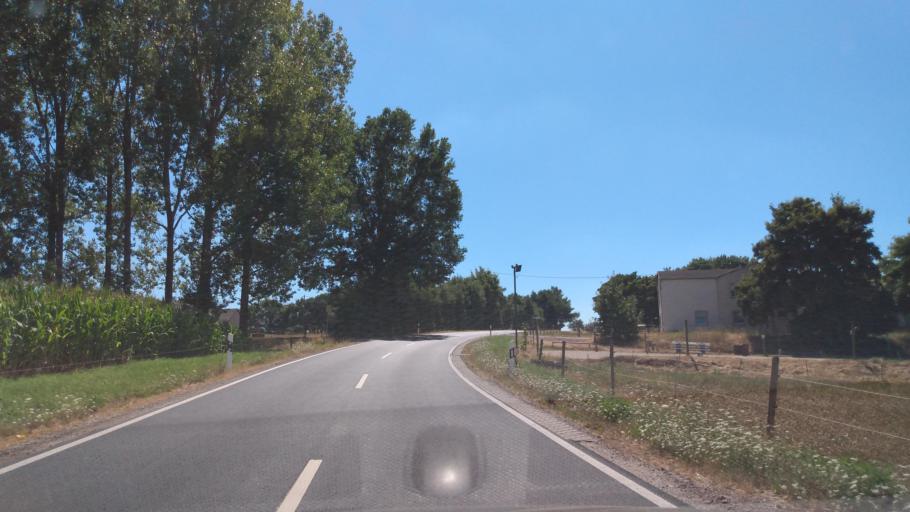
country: DE
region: Rheinland-Pfalz
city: Musweiler
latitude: 50.0092
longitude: 6.7792
